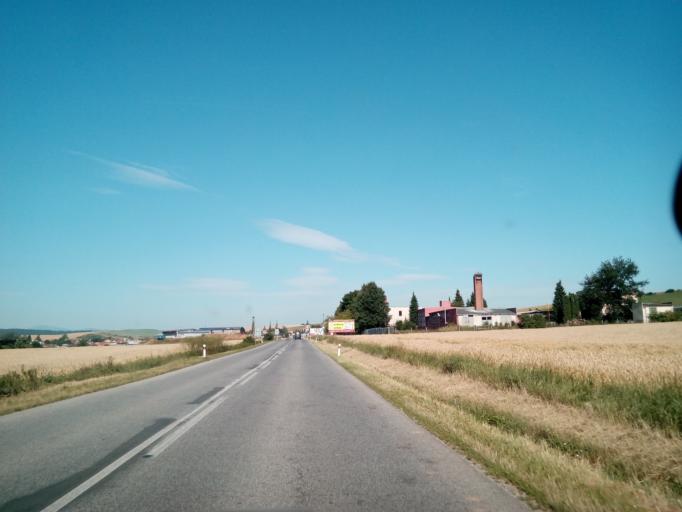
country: SK
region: Kosicky
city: Krompachy
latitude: 48.9455
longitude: 20.8119
